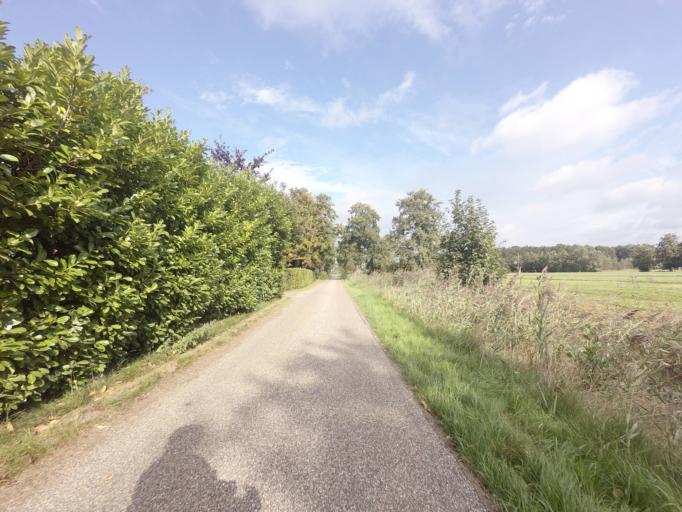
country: NL
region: Friesland
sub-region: Gemeente Heerenveen
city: Jubbega
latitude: 52.9911
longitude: 6.1103
